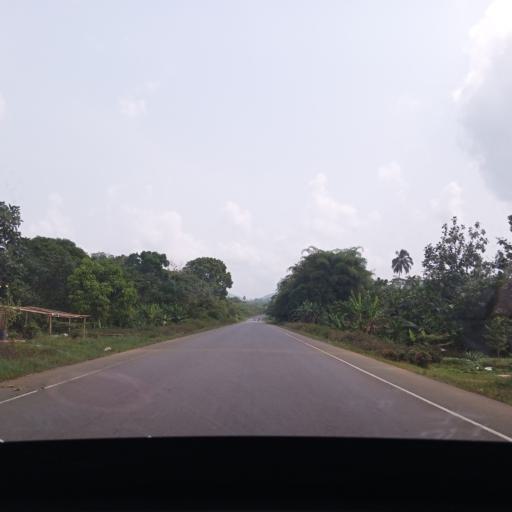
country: LR
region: Margibi
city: Kakata
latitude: 6.2538
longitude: -10.3103
